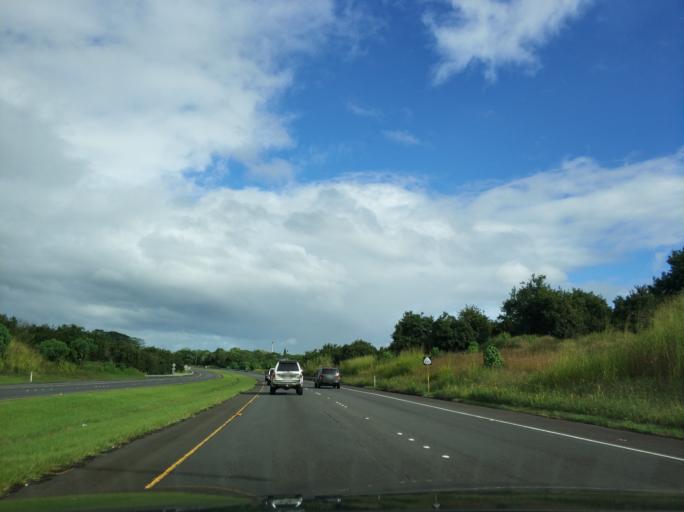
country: US
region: Hawaii
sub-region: Hawaii County
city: Kea'au
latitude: 19.6175
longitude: -155.0299
